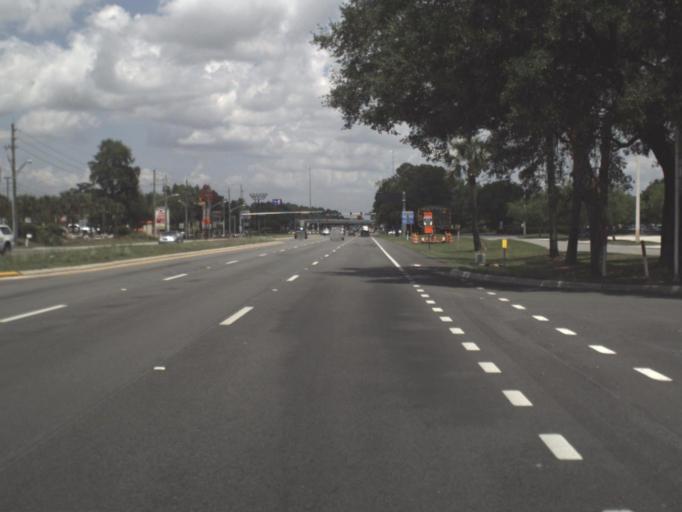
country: US
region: Florida
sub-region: Saint Johns County
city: Fruit Cove
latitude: 30.1800
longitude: -81.5532
